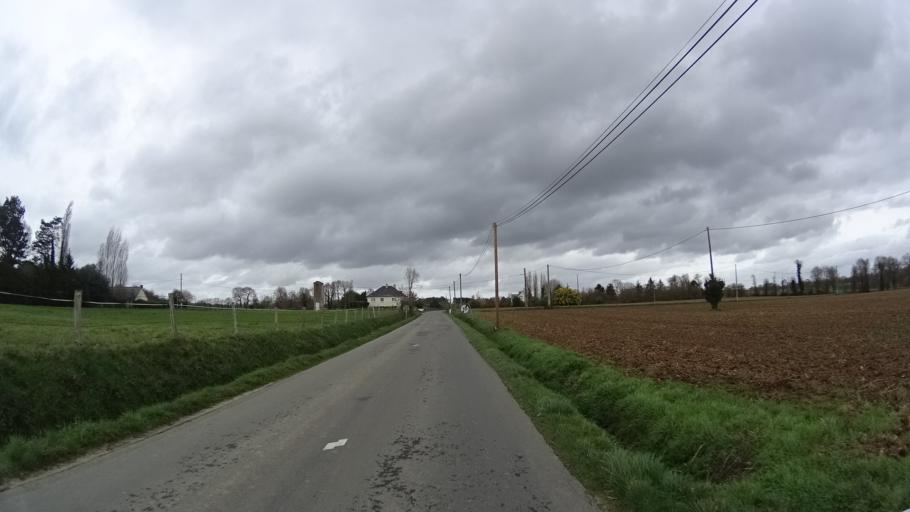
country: FR
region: Brittany
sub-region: Departement d'Ille-et-Vilaine
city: Saint-Gilles
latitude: 48.1652
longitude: -1.8301
